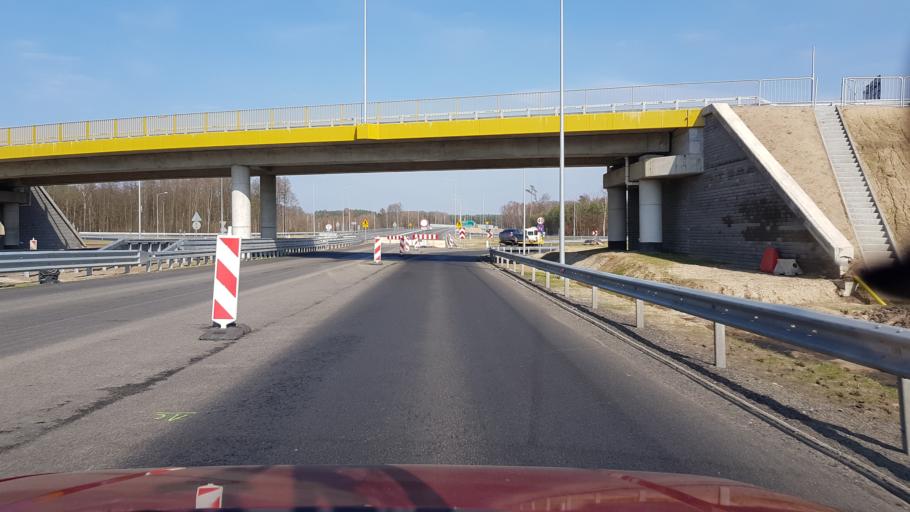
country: PL
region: West Pomeranian Voivodeship
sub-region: Powiat goleniowski
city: Osina
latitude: 53.6317
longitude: 14.9942
